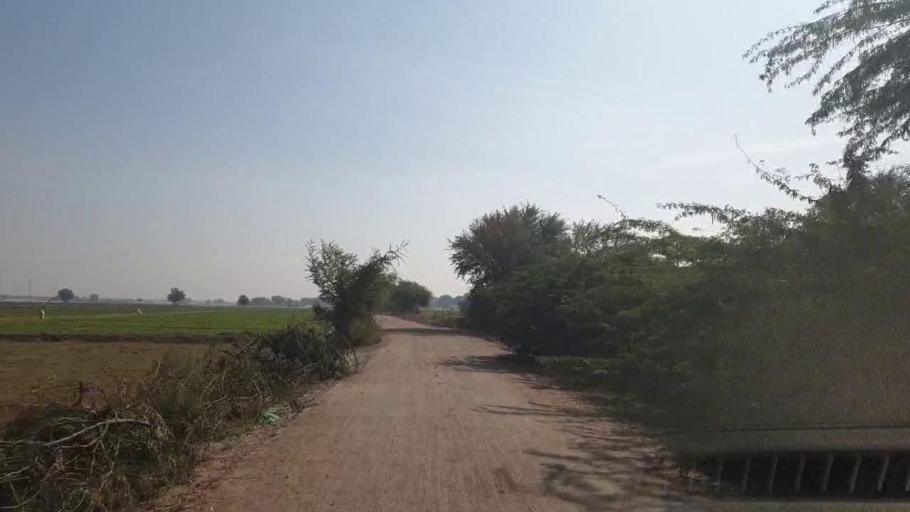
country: PK
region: Sindh
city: Matiari
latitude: 25.6757
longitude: 68.3581
